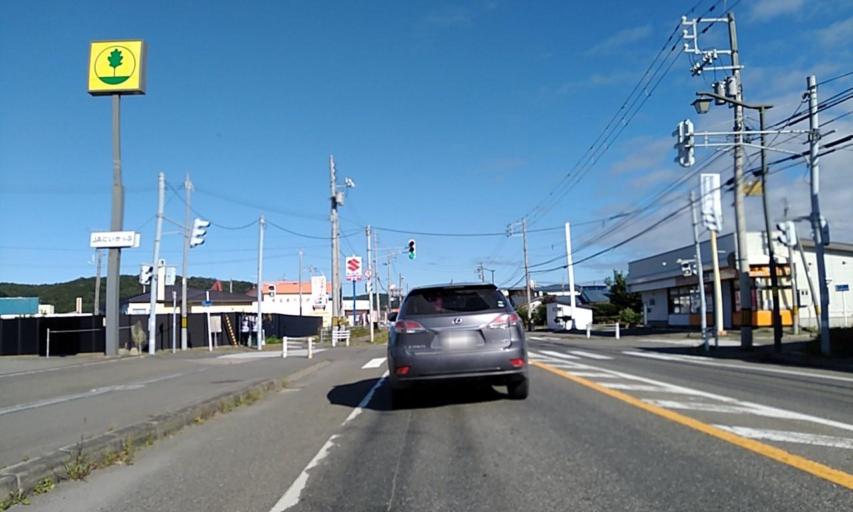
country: JP
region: Hokkaido
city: Shizunai-furukawacho
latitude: 42.3631
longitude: 142.3167
